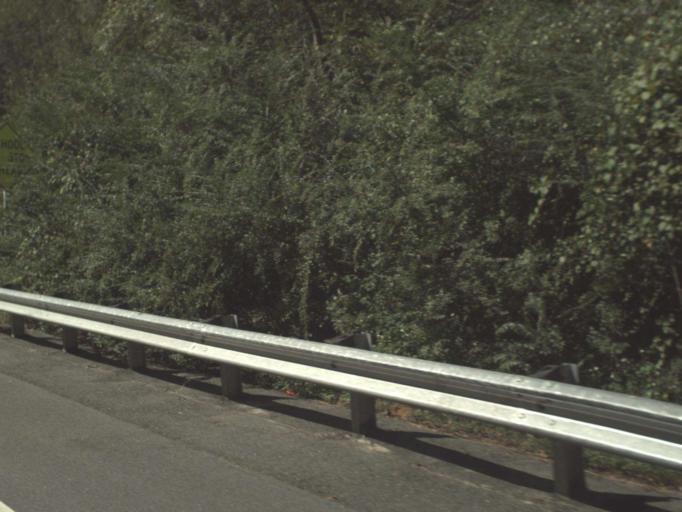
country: US
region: Alabama
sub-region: Covington County
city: Florala
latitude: 30.9645
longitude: -86.4227
